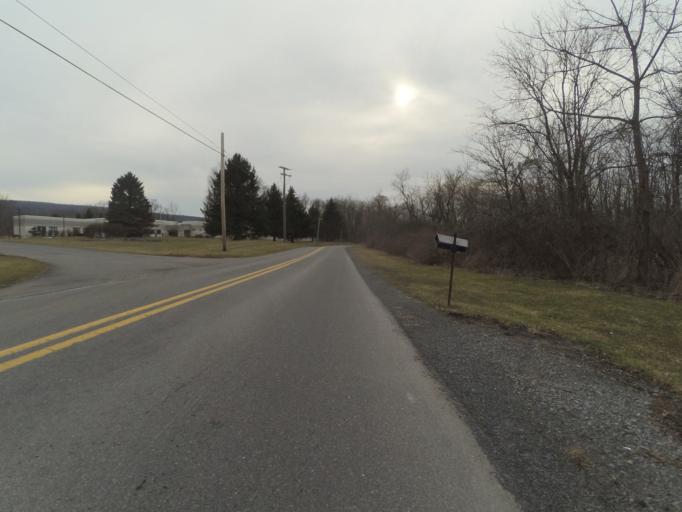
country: US
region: Pennsylvania
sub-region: Centre County
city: State College
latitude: 40.7728
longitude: -77.8333
